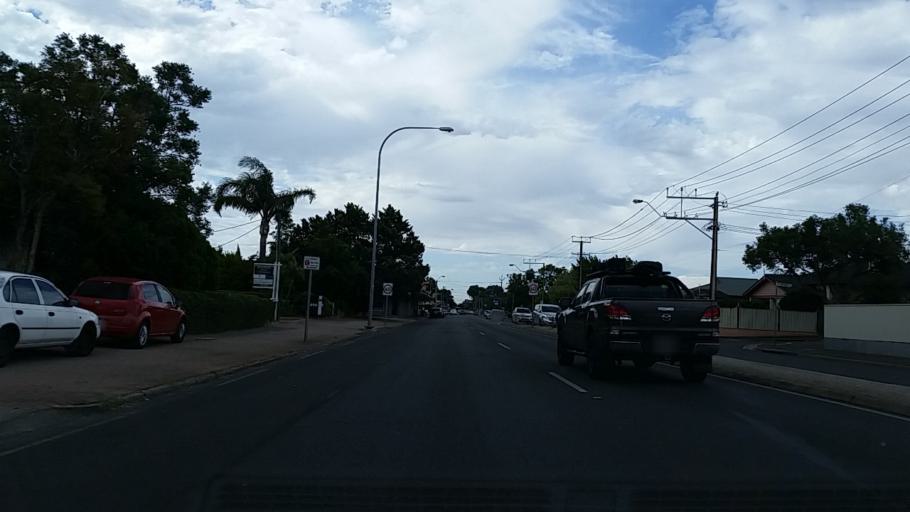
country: AU
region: South Australia
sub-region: Mitcham
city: Clarence Gardens
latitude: -34.9767
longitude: 138.5915
